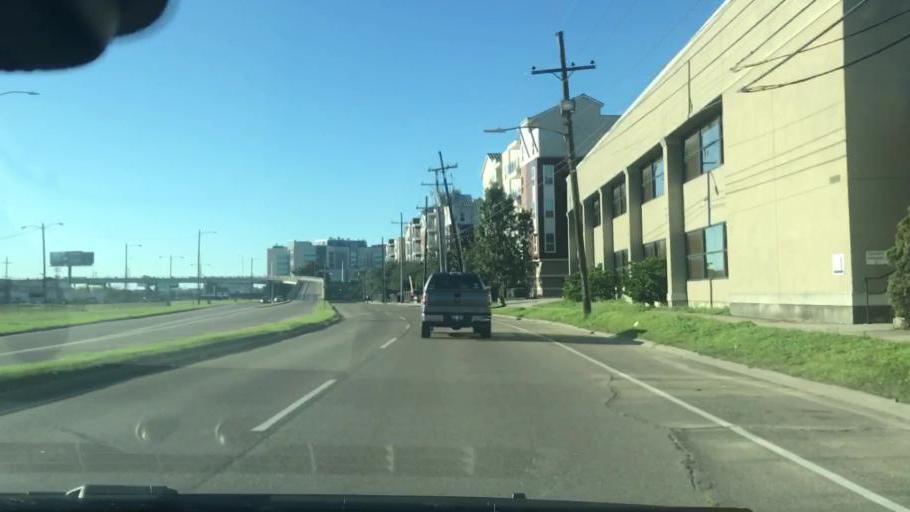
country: US
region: Louisiana
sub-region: Orleans Parish
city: New Orleans
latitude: 29.9575
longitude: -90.0899
